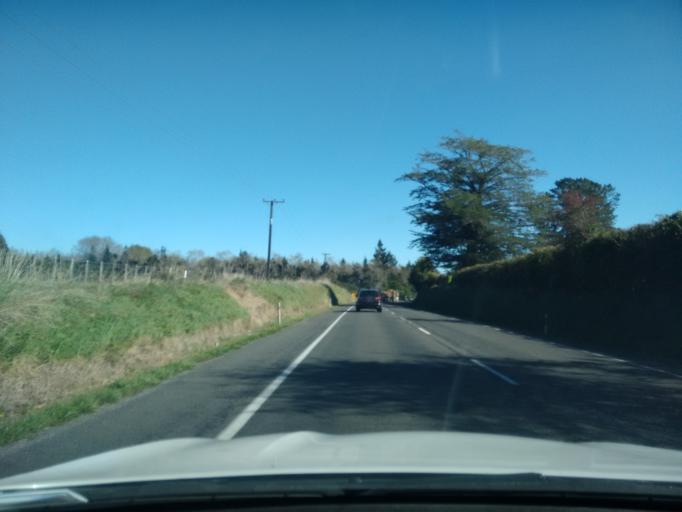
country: NZ
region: Taranaki
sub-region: New Plymouth District
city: New Plymouth
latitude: -39.1501
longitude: 174.1528
